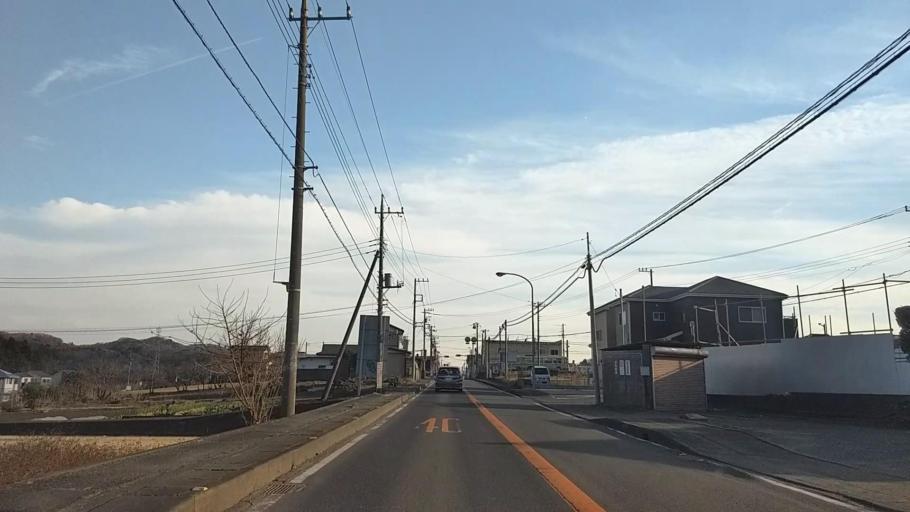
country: JP
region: Kanagawa
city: Zama
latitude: 35.5144
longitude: 139.2988
